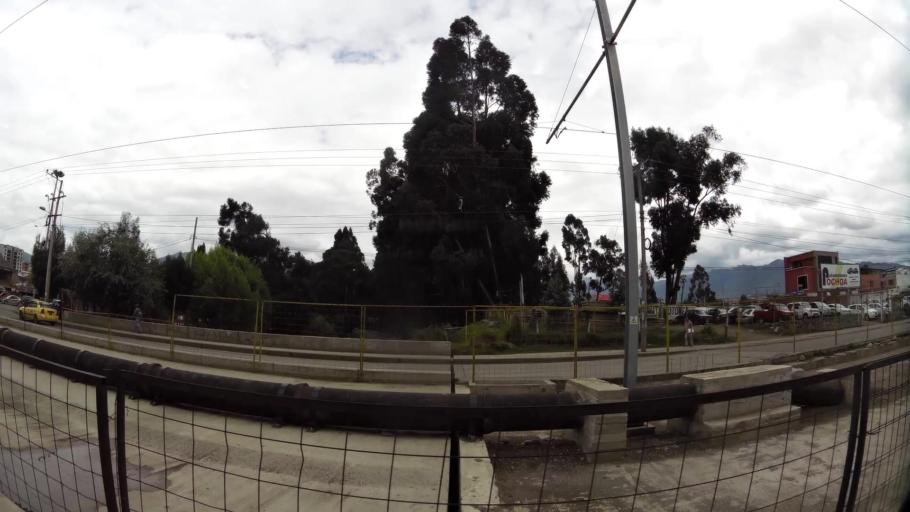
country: EC
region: Azuay
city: Cuenca
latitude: -2.9065
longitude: -79.0331
